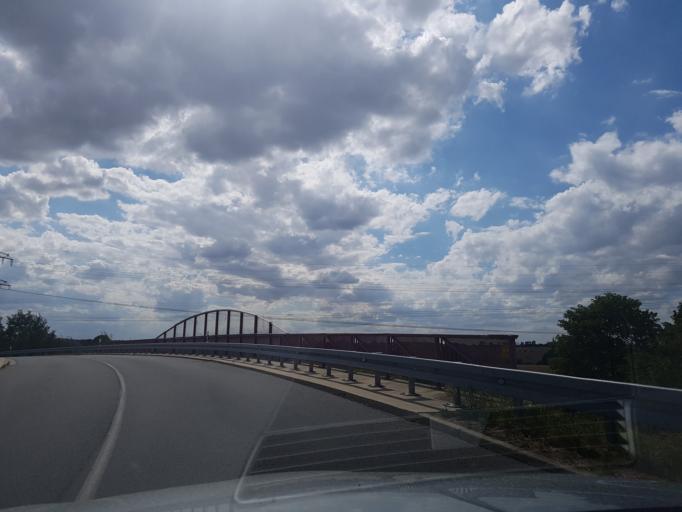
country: DE
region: Saxony
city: Priestewitz
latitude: 51.2385
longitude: 13.5448
